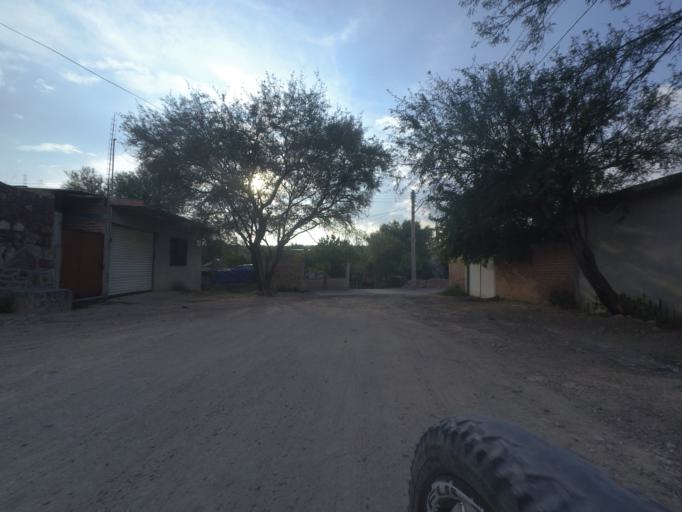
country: MX
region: Aguascalientes
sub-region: Aguascalientes
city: Los Canos
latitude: 21.7772
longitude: -102.3739
